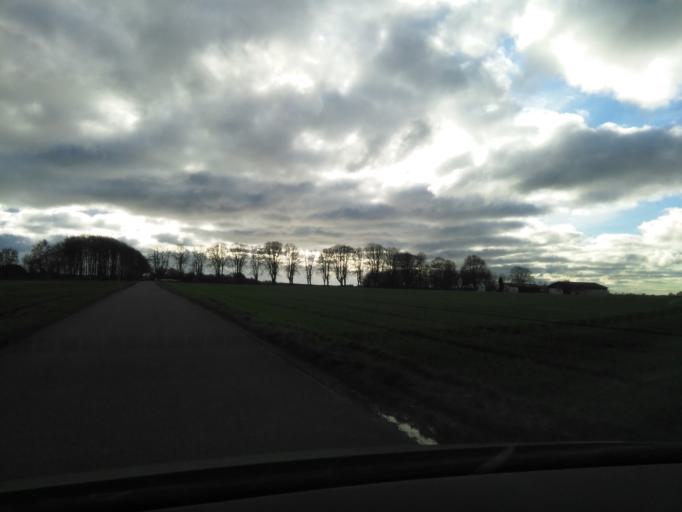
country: DK
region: Central Jutland
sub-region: Odder Kommune
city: Odder
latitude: 55.9218
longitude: 10.1868
